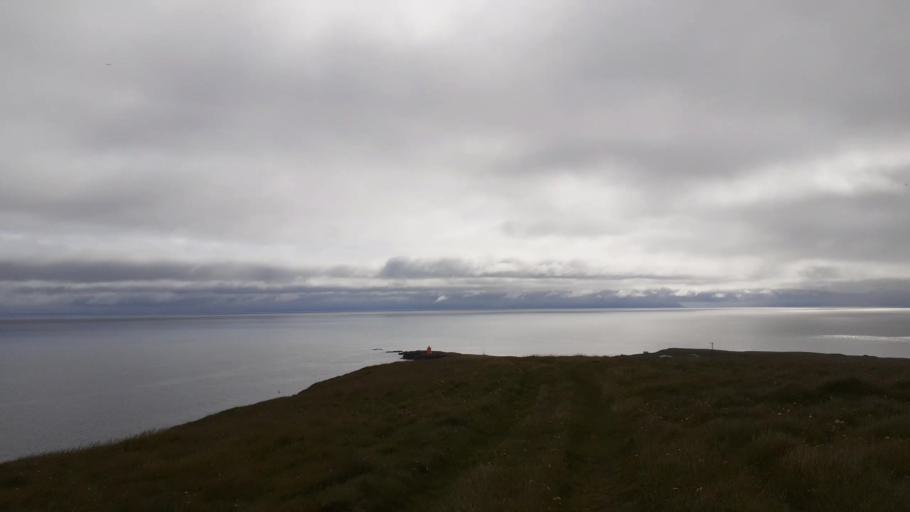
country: IS
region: Northeast
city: Dalvik
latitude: 66.5362
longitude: -17.9818
